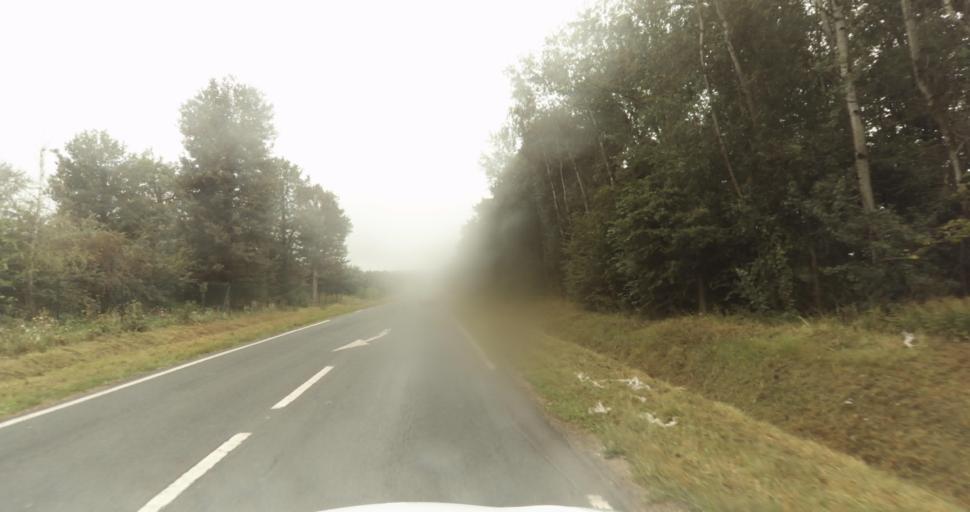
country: FR
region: Haute-Normandie
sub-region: Departement de l'Eure
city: Normanville
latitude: 49.0934
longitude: 1.1760
